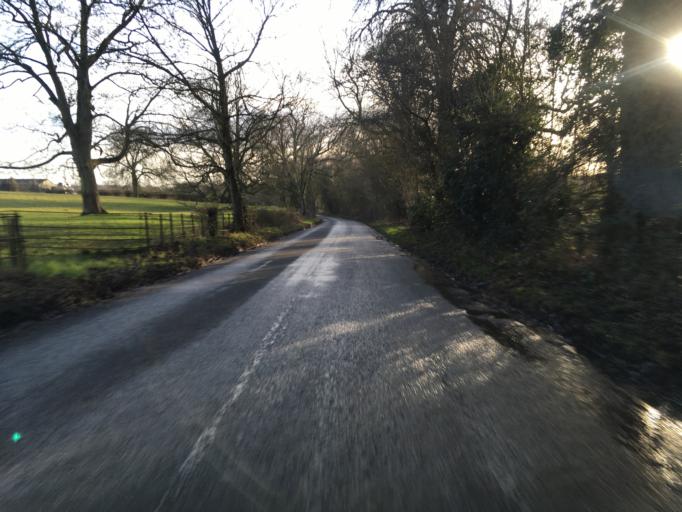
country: GB
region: England
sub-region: Warwickshire
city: Stratford-upon-Avon
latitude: 52.2261
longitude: -1.6894
